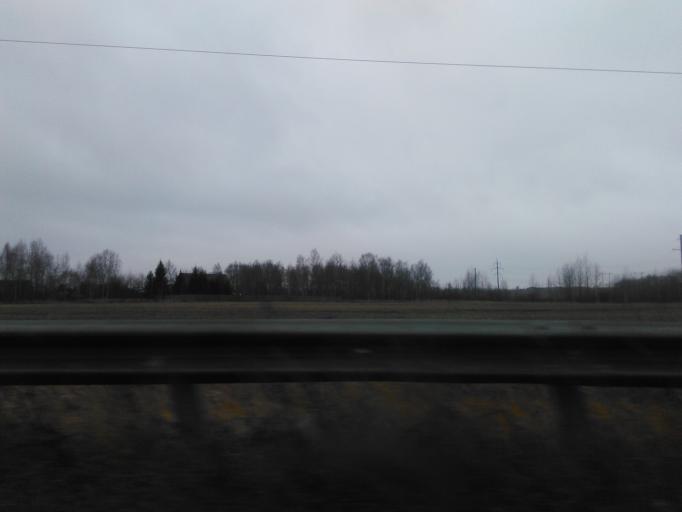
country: RU
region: Moskovskaya
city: Ashukino
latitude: 56.1562
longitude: 37.9621
